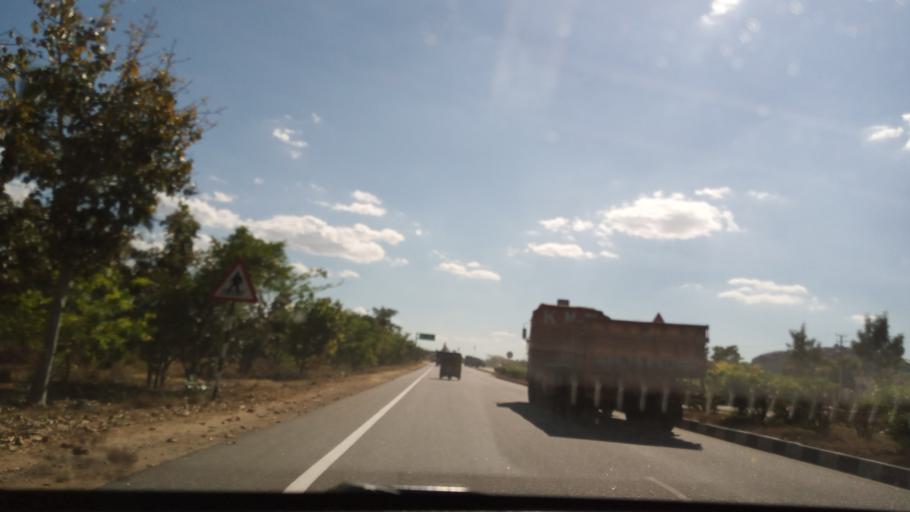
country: IN
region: Karnataka
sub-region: Kolar
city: Mulbagal
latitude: 13.1808
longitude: 78.4173
